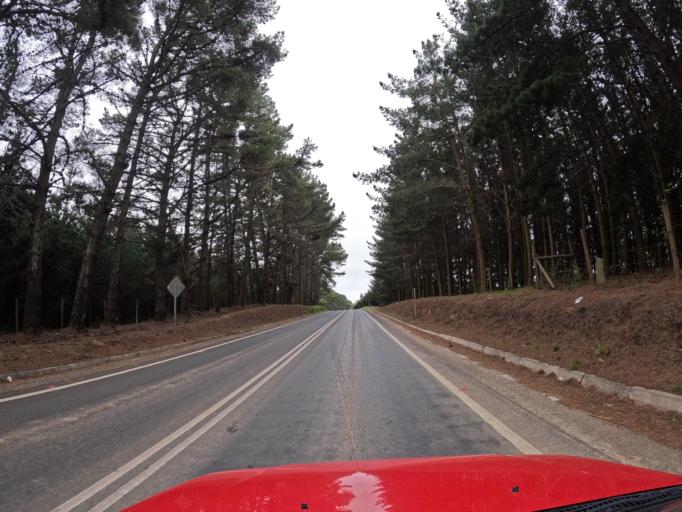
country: CL
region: O'Higgins
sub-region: Provincia de Colchagua
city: Santa Cruz
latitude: -34.5747
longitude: -72.0151
